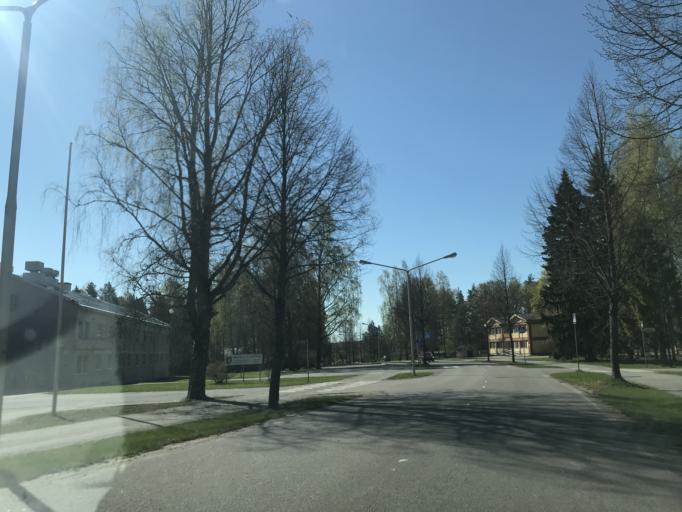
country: FI
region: Paijanne Tavastia
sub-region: Lahti
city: Orimattila
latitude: 60.8100
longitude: 25.7361
